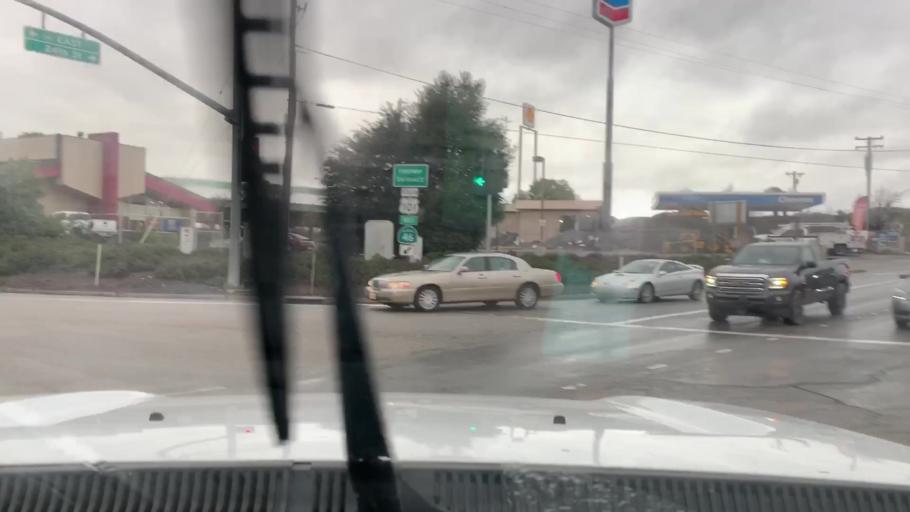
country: US
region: California
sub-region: San Luis Obispo County
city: Paso Robles
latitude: 35.6424
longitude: -120.6855
